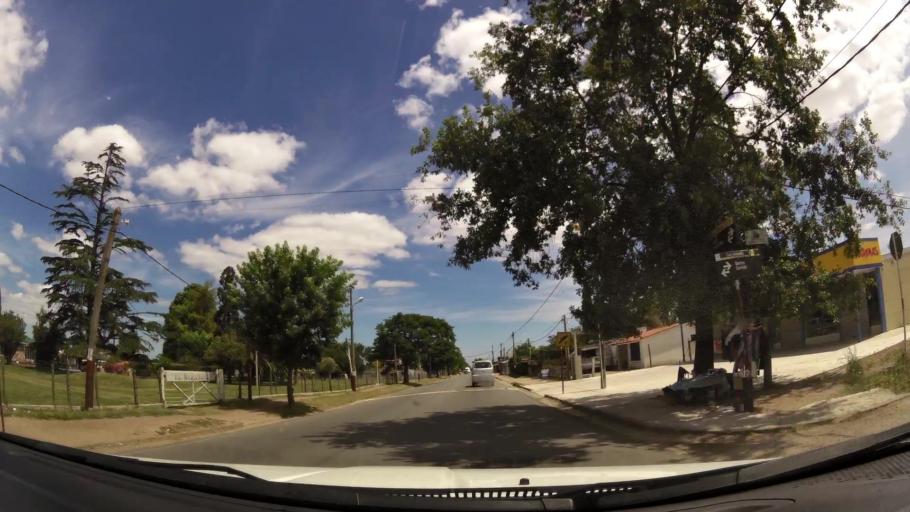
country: UY
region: San Jose
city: Delta del Tigre
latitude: -34.7442
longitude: -56.4520
